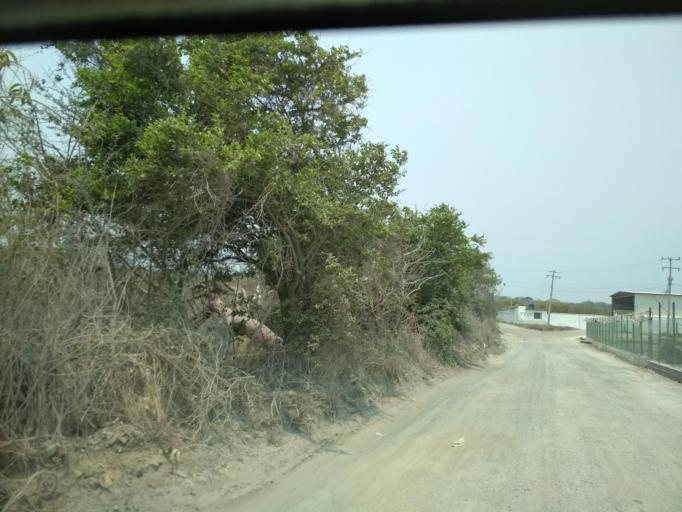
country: MX
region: Veracruz
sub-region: Veracruz
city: Delfino Victoria (Santa Fe)
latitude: 19.2256
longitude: -96.2589
